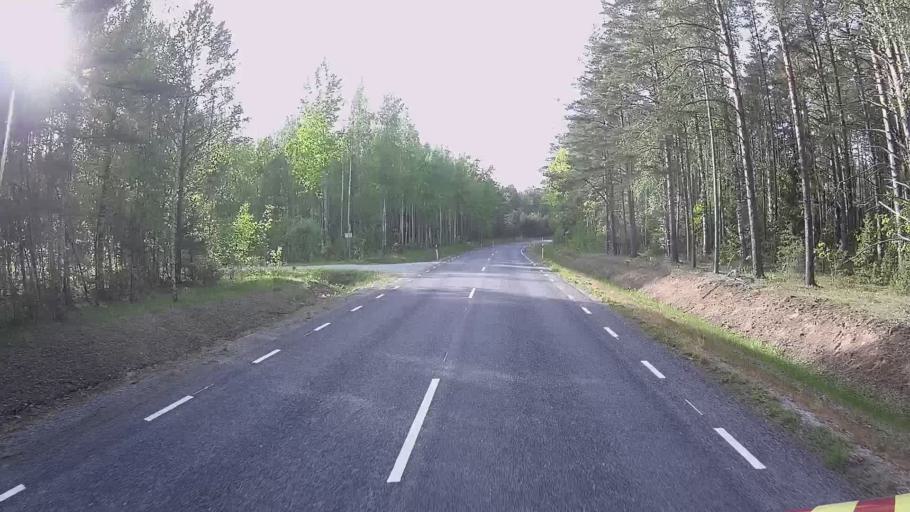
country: EE
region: Jogevamaa
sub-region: Mustvee linn
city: Mustvee
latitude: 58.9905
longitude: 27.1597
